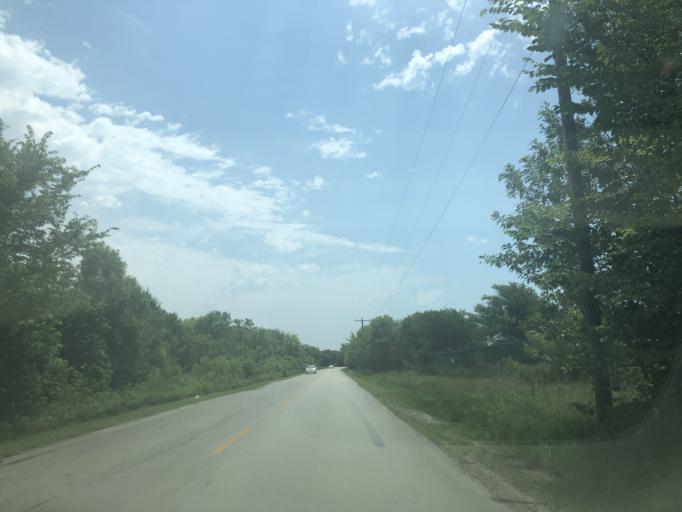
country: US
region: Texas
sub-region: Dallas County
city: Irving
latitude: 32.7867
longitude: -96.9375
